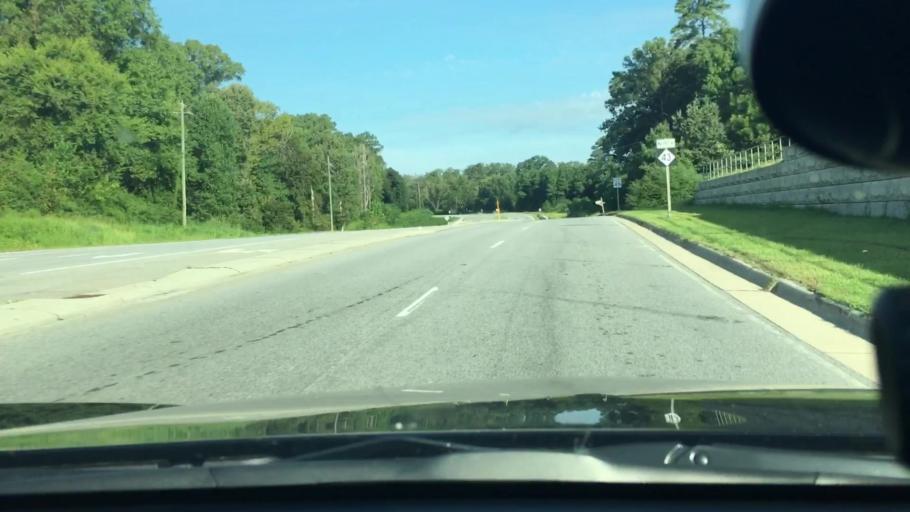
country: US
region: North Carolina
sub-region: Pitt County
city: Greenville
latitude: 35.6216
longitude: -77.4174
